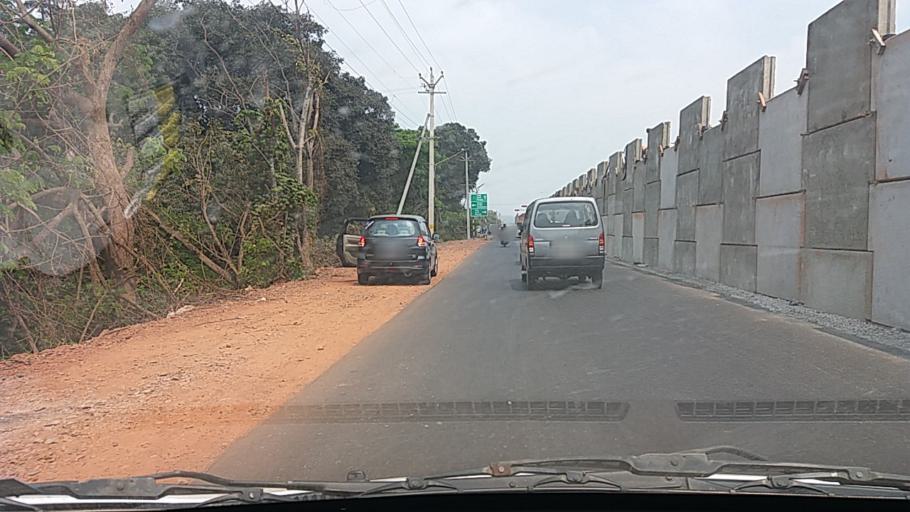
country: IN
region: Goa
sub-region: North Goa
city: Bambolim
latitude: 15.4772
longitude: 73.8489
